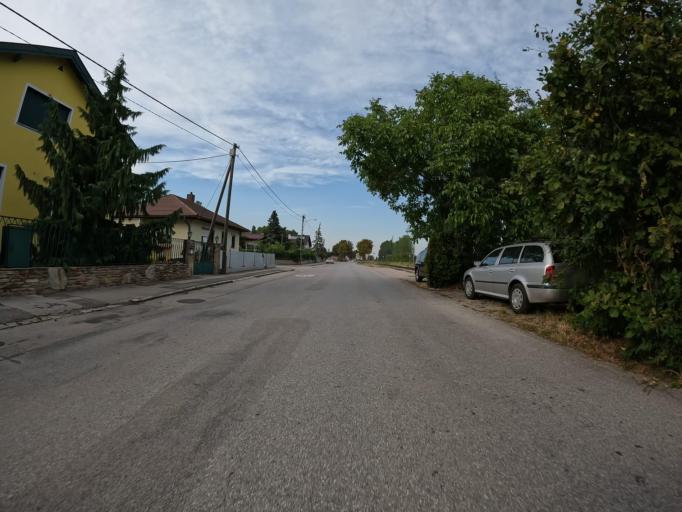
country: AT
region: Lower Austria
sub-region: Politischer Bezirk Baden
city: Traiskirchen
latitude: 48.0149
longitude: 16.3007
